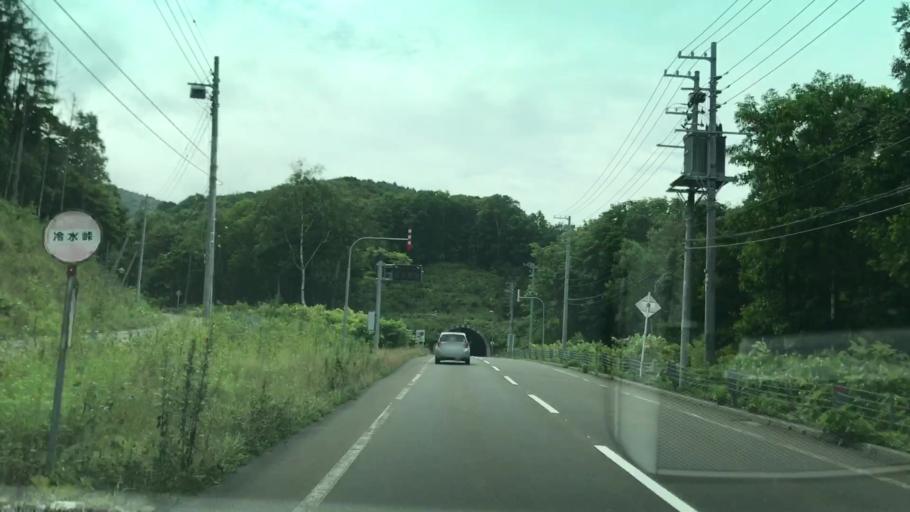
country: JP
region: Hokkaido
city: Yoichi
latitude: 43.1252
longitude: 140.8287
